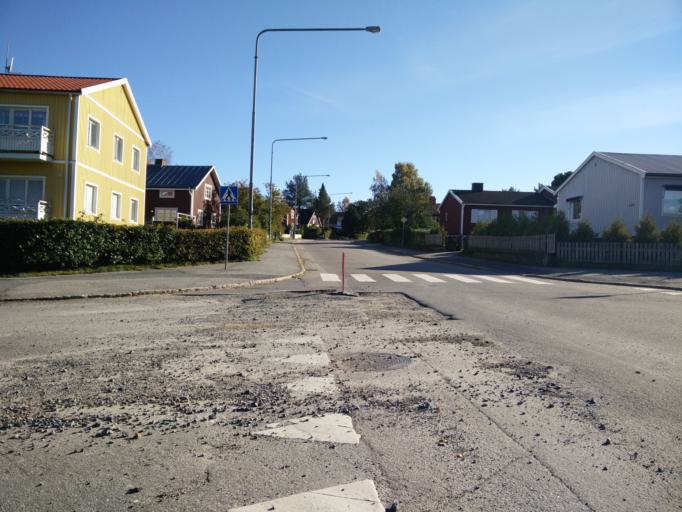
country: SE
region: Vaesternorrland
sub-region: Haernoesands Kommun
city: Haernoesand
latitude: 62.6390
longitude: 17.9586
